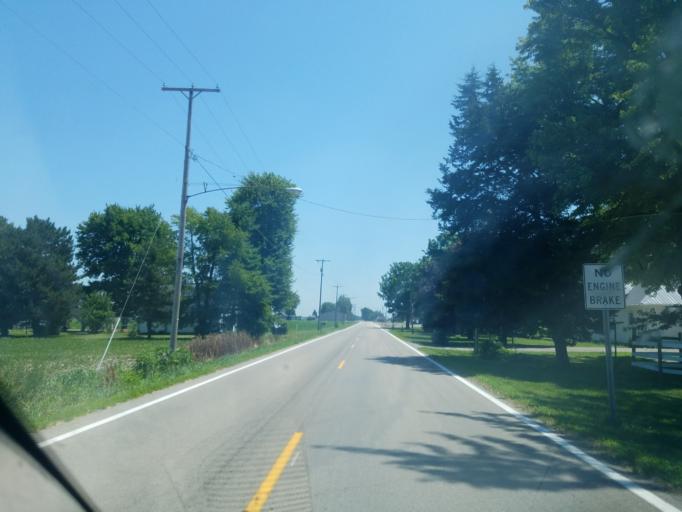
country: US
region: Ohio
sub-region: Allen County
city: Spencerville
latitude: 40.7426
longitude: -84.4796
